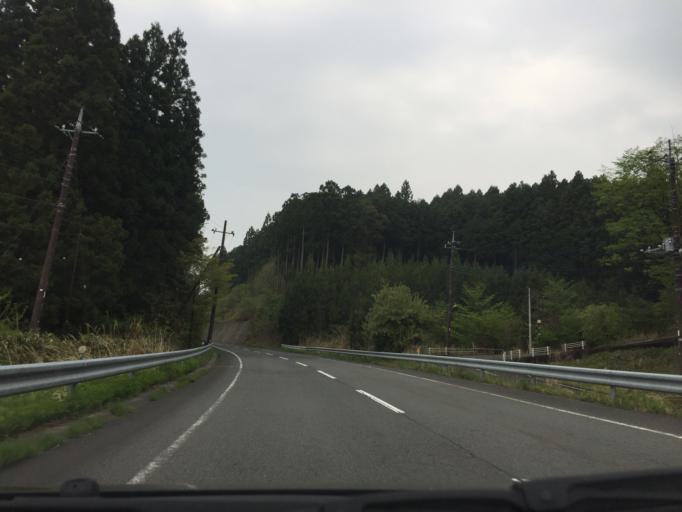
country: JP
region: Tochigi
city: Imaichi
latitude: 36.8603
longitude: 139.7239
